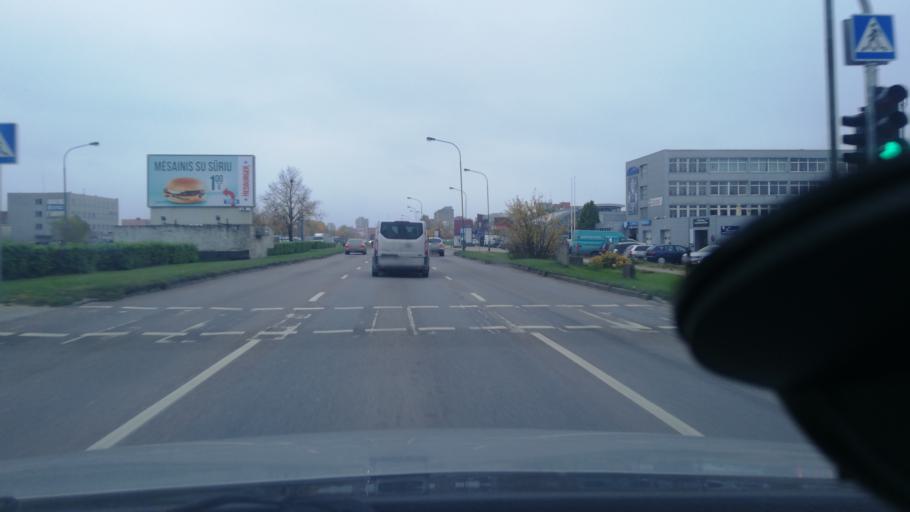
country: LT
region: Klaipedos apskritis
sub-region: Klaipeda
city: Klaipeda
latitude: 55.6839
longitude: 21.1846
